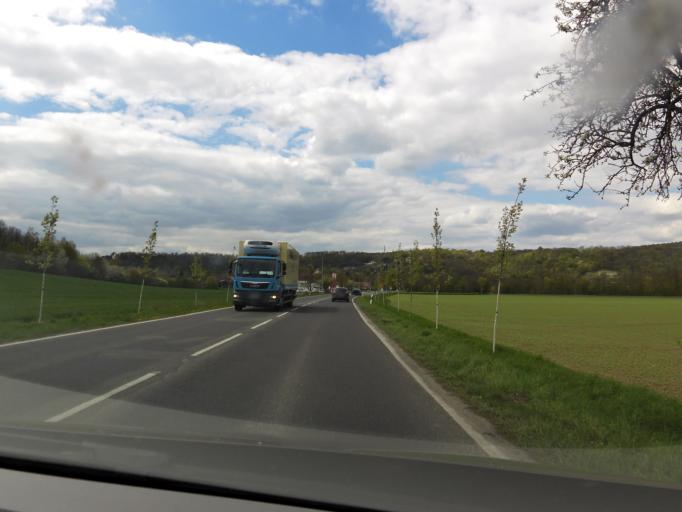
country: DE
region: Saxony-Anhalt
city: Bad Kosen
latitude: 51.1392
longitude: 11.7333
